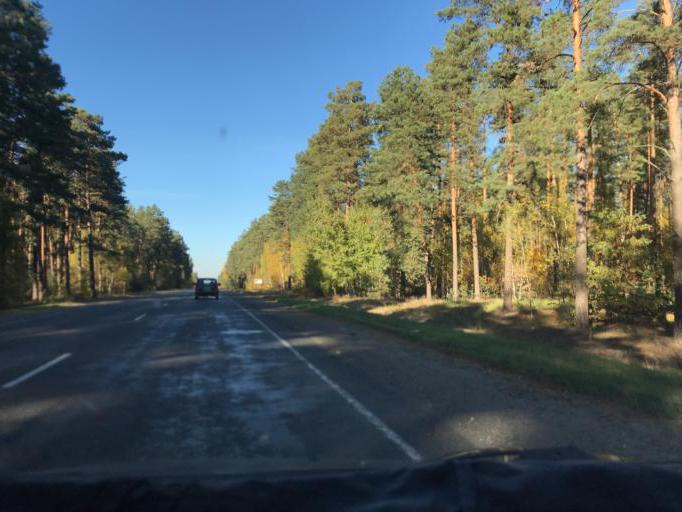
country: BY
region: Gomel
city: Kalinkavichy
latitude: 52.0590
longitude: 29.3611
